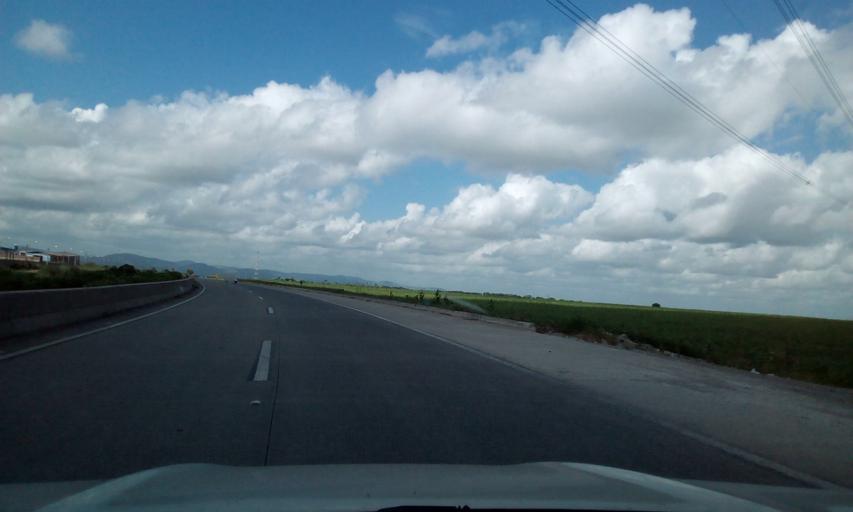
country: BR
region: Alagoas
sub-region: Messias
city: Messias
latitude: -9.4007
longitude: -35.8367
